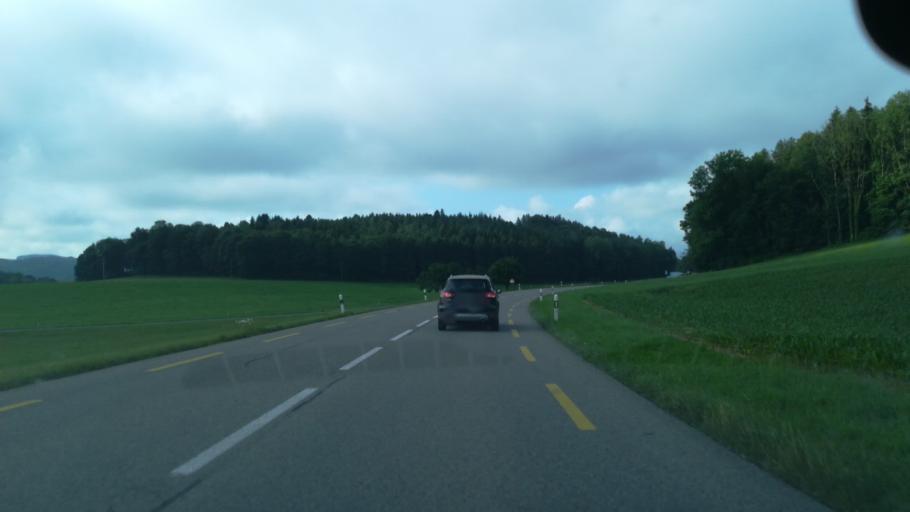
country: CH
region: Saint Gallen
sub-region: Wahlkreis St. Gallen
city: Waldkirch
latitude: 47.4921
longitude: 9.2587
